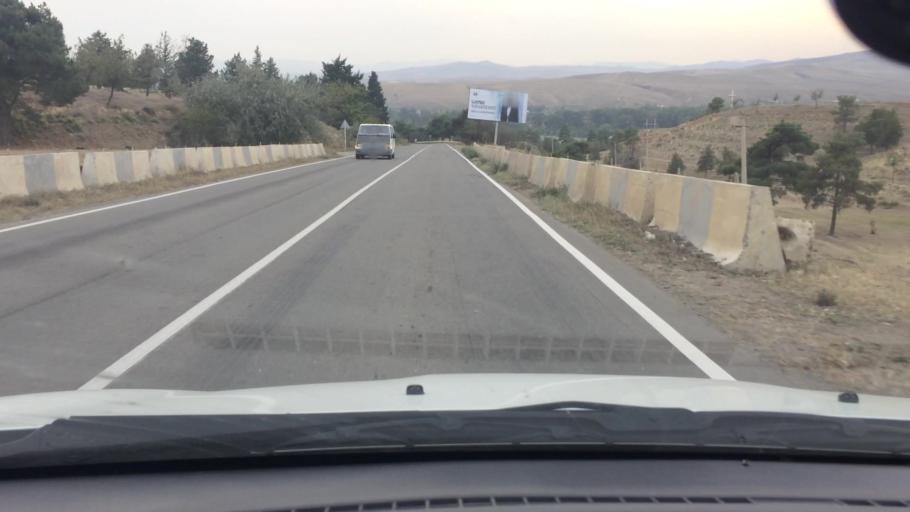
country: GE
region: Kvemo Kartli
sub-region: Gardabani
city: Gardabani
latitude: 41.3465
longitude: 45.0684
